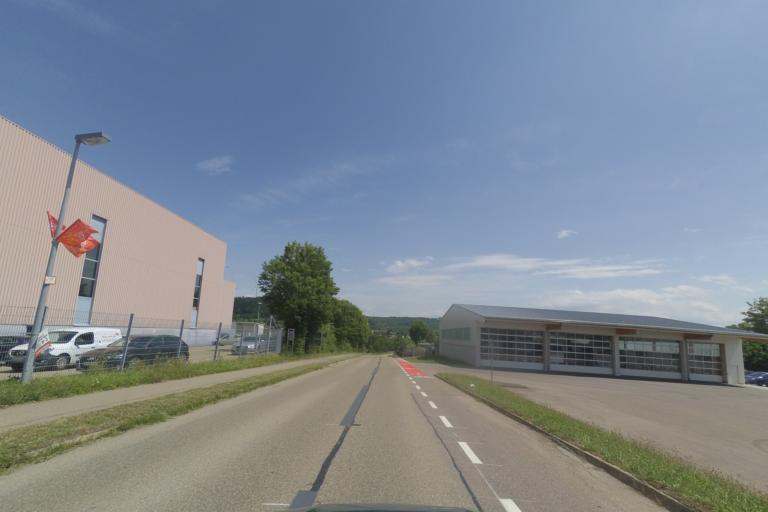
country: DE
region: Baden-Wuerttemberg
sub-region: Regierungsbezirk Stuttgart
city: Gaildorf
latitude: 48.9979
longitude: 9.7757
